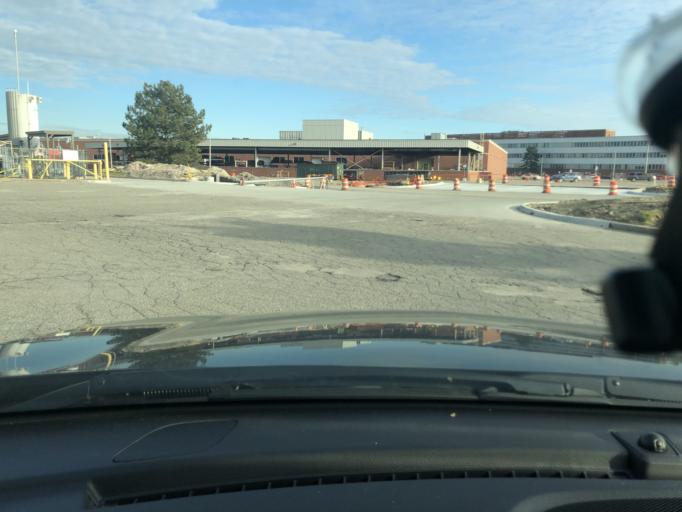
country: US
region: Michigan
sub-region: Wayne County
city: Allen Park
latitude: 42.2945
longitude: -83.2339
